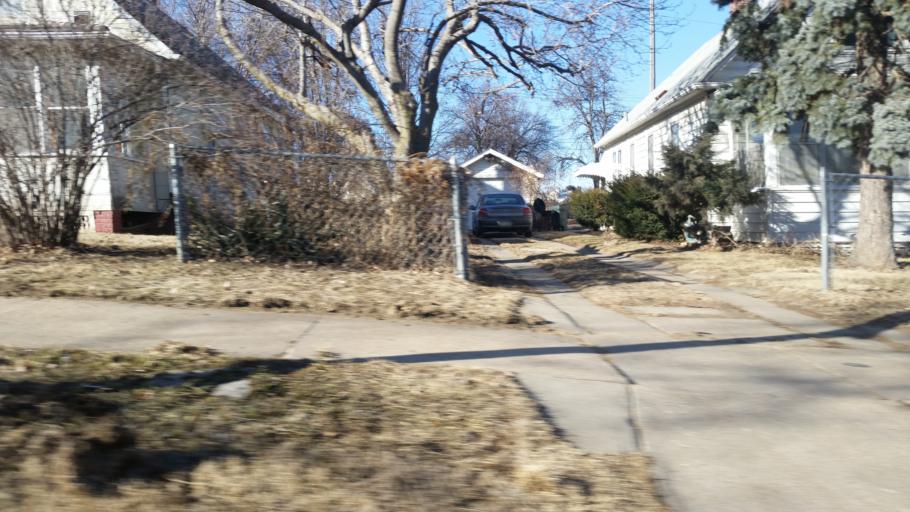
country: US
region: Nebraska
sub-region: Douglas County
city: Omaha
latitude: 41.2230
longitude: -95.9306
